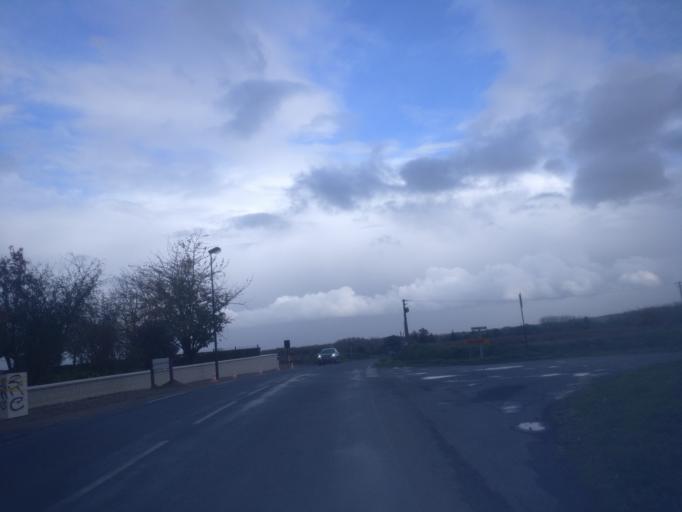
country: FR
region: Brittany
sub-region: Departement d'Ille-et-Vilaine
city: Breal-sous-Montfort
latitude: 48.0463
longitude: -1.8532
